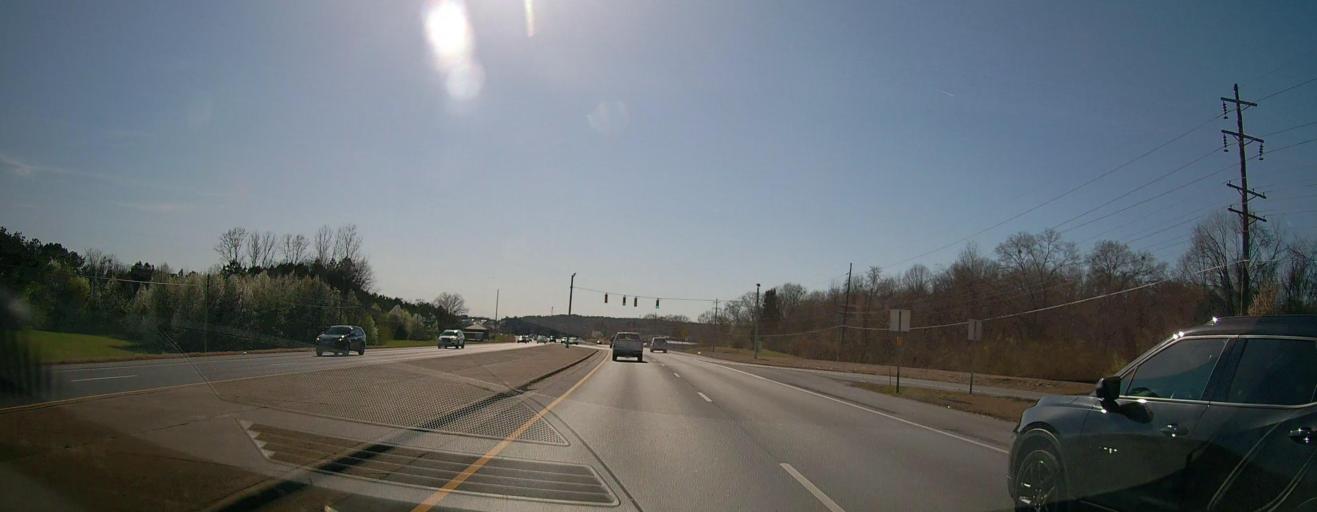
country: US
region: Alabama
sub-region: Lauderdale County
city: Killen
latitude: 34.8553
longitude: -87.5565
